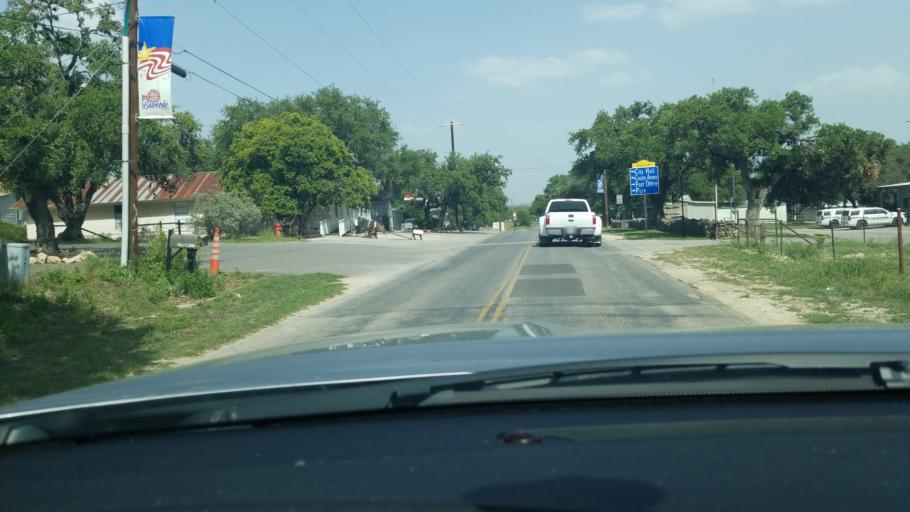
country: US
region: Texas
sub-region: Comal County
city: Bulverde
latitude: 29.7445
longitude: -98.4547
